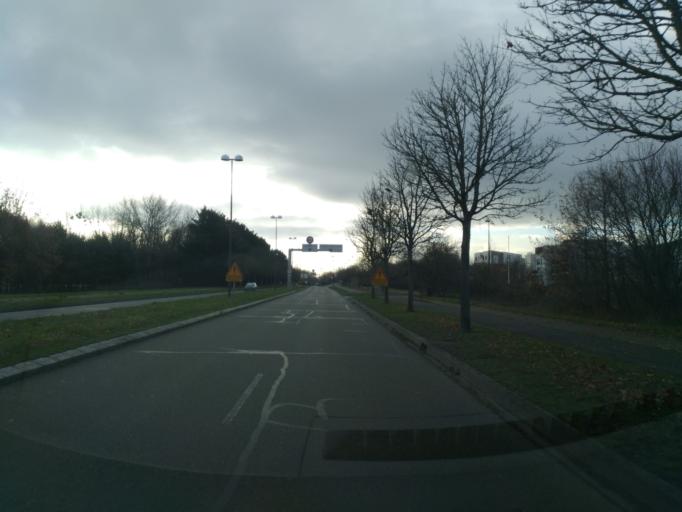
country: FR
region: Ile-de-France
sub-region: Departement des Yvelines
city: Guyancourt
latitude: 48.7642
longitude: 2.0767
